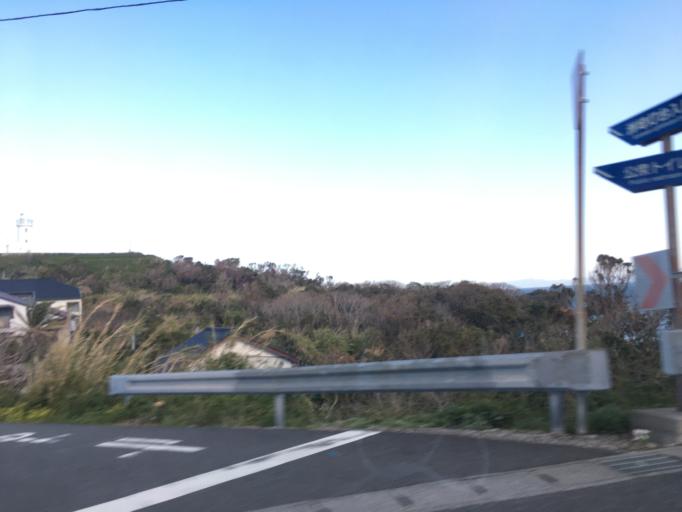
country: JP
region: Chiba
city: Tateyama
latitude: 34.9739
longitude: 139.7584
